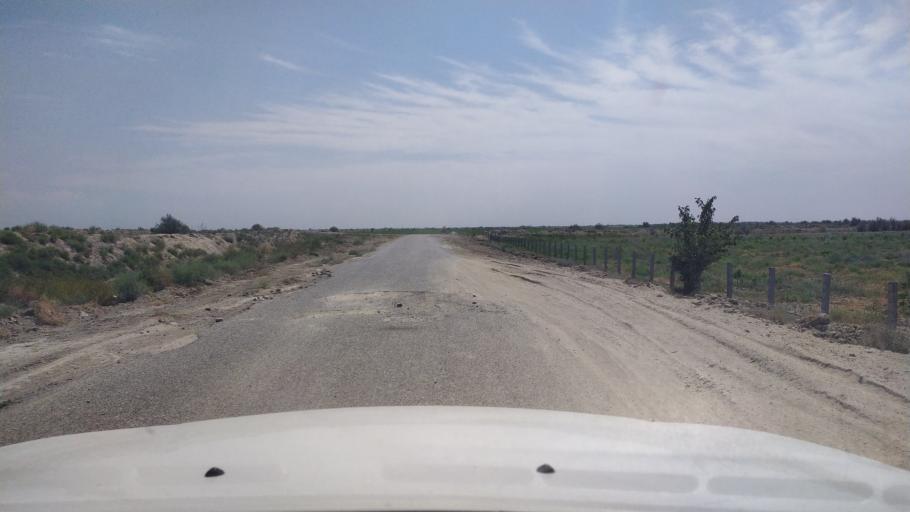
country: UZ
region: Namangan
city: Toshbuloq
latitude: 40.7895
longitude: 71.5615
